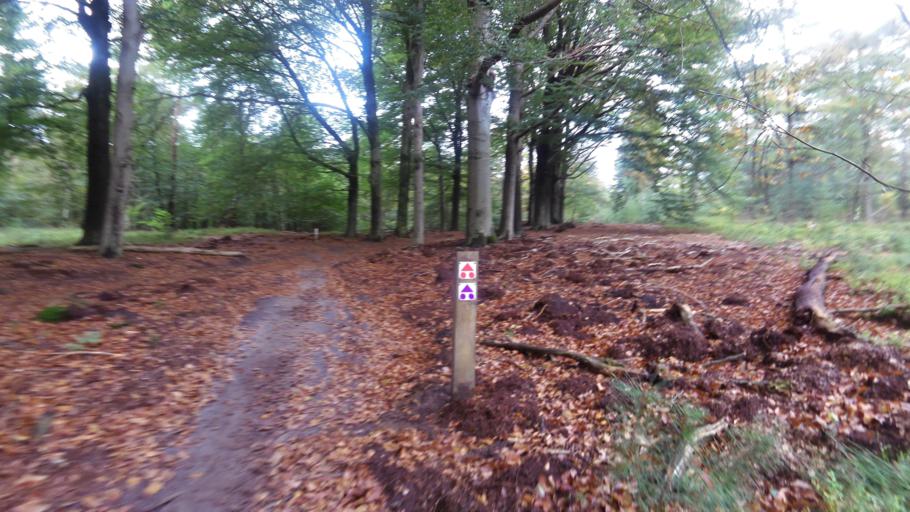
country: NL
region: Gelderland
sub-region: Gemeente Ede
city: Wekerom
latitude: 52.0725
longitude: 5.7161
